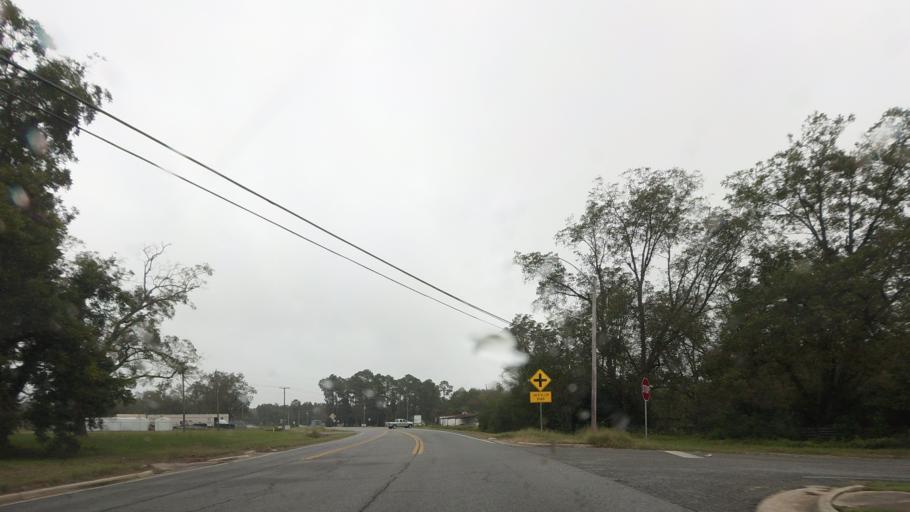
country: US
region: Georgia
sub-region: Ben Hill County
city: Fitzgerald
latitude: 31.7296
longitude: -83.2465
